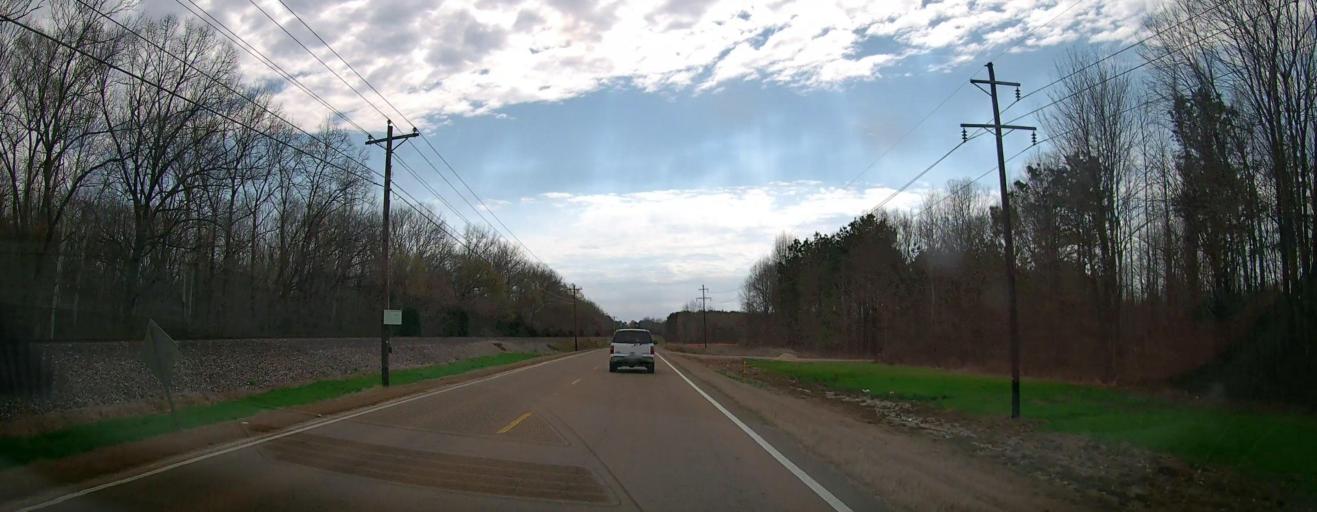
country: US
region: Mississippi
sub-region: Marshall County
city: Byhalia
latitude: 34.8970
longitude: -89.7394
